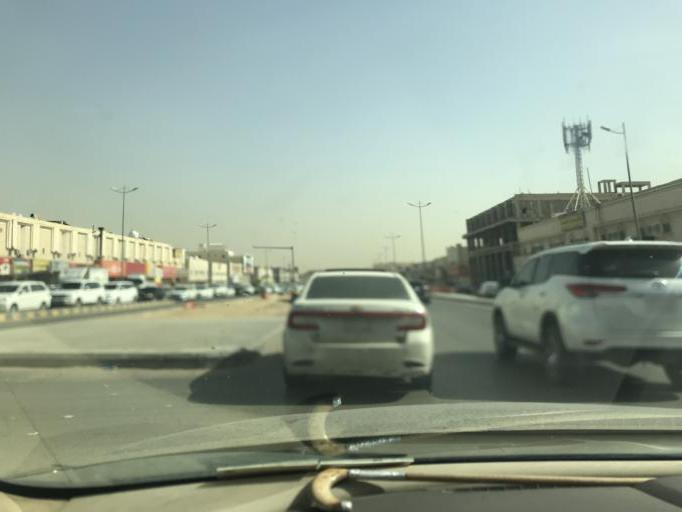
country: SA
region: Ar Riyad
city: Riyadh
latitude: 24.7997
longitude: 46.7405
